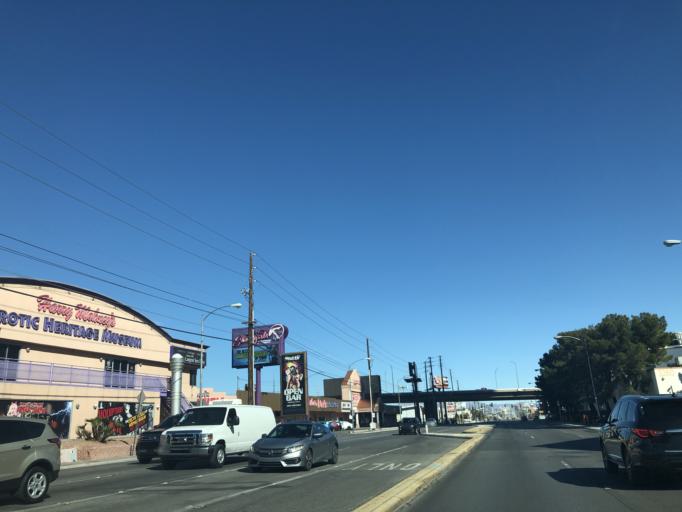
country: US
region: Nevada
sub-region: Clark County
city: Paradise
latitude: 36.1297
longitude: -115.1742
